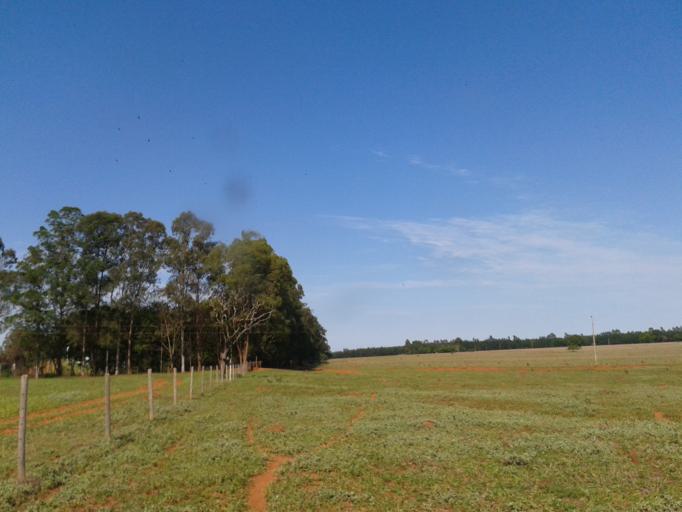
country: BR
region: Minas Gerais
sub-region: Centralina
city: Centralina
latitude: -18.7199
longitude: -49.1556
